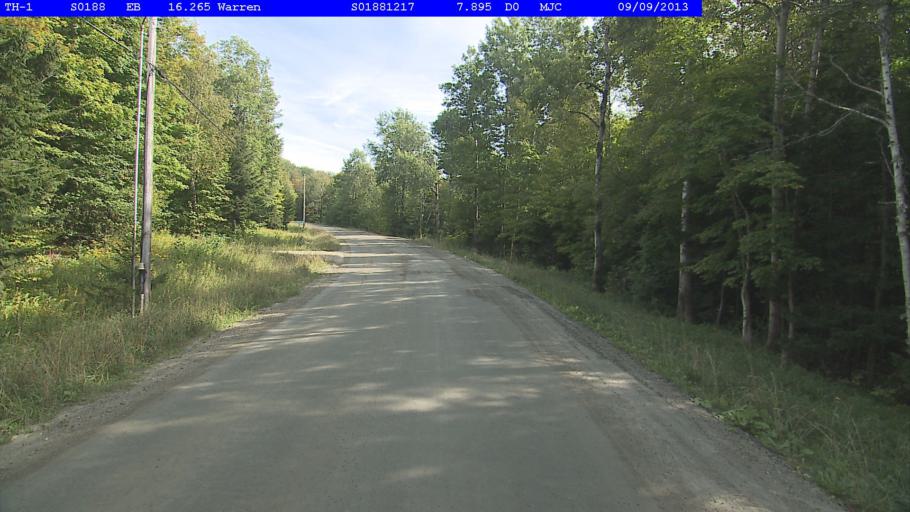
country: US
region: Vermont
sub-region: Washington County
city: Northfield
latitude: 44.1076
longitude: -72.7988
